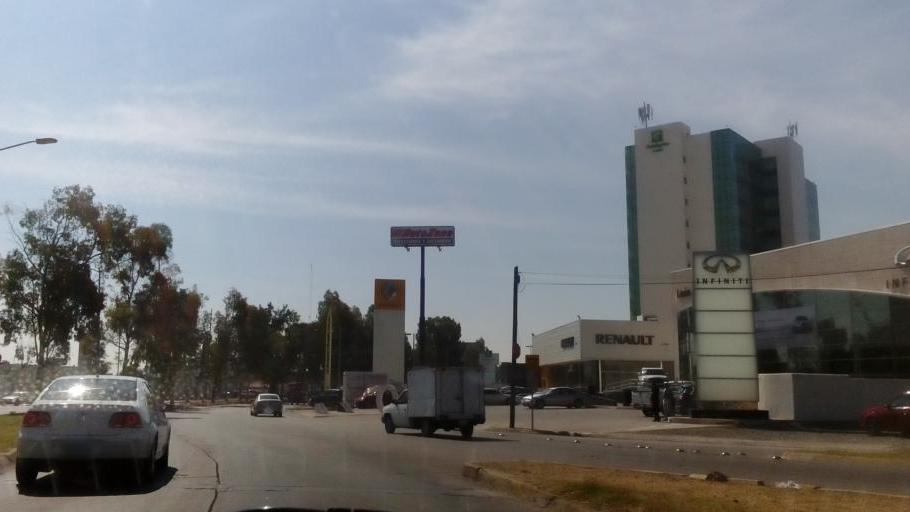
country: MX
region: Guanajuato
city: Leon
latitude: 21.1544
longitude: -101.6852
